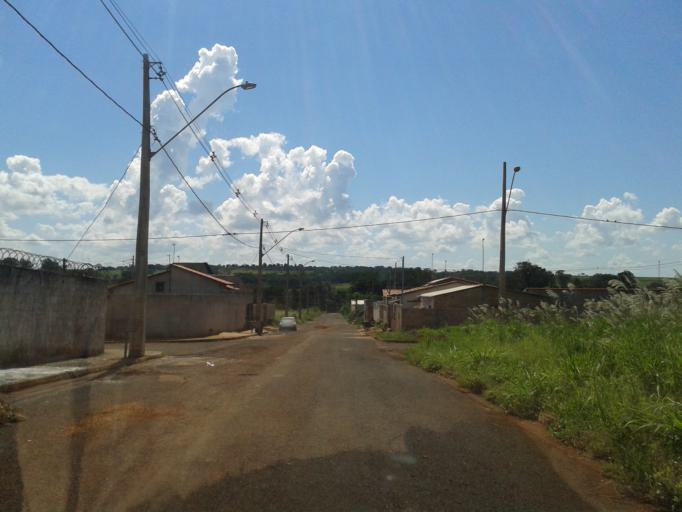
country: BR
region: Goias
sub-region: Itumbiara
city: Itumbiara
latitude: -18.4231
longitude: -49.1851
